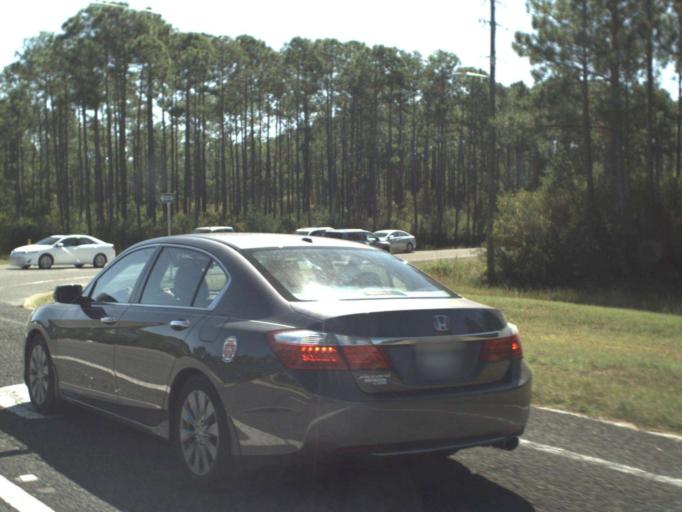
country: US
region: Florida
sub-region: Walton County
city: Seaside
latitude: 30.3694
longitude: -86.1961
